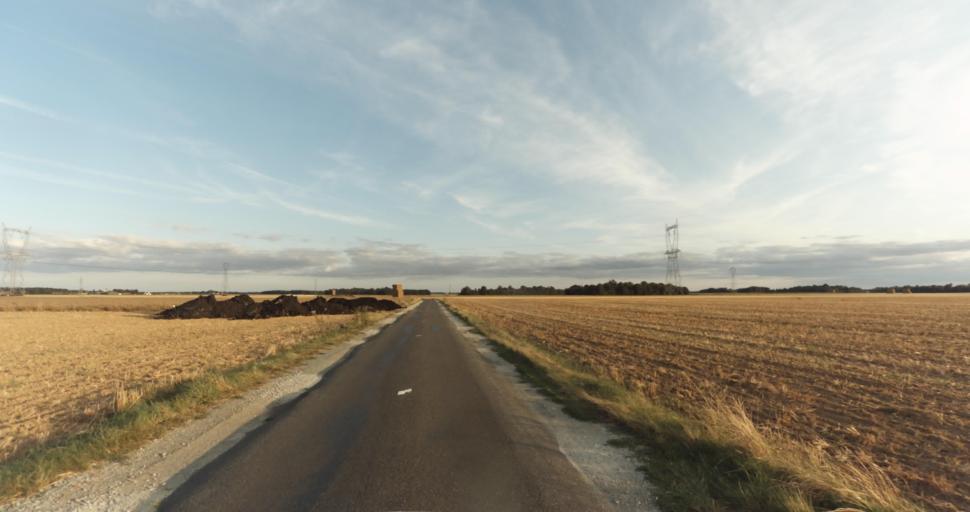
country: FR
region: Haute-Normandie
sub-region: Departement de l'Eure
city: Saint-Germain-sur-Avre
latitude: 48.8572
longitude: 1.2557
